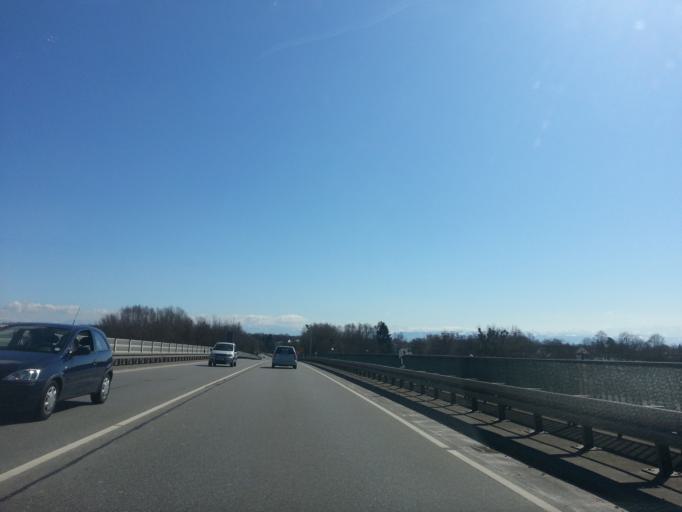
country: DE
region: Baden-Wuerttemberg
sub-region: Tuebingen Region
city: Friedrichshafen
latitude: 47.6599
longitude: 9.4975
